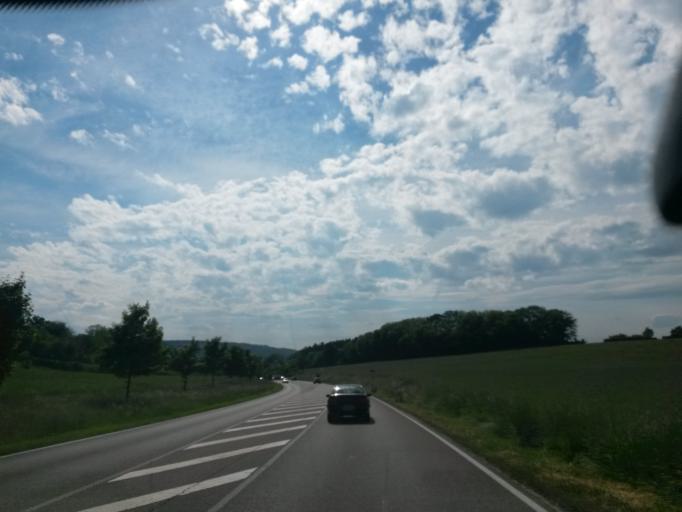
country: DE
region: Baden-Wuerttemberg
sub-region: Regierungsbezirk Stuttgart
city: Weil der Stadt
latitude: 48.7492
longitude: 8.8880
